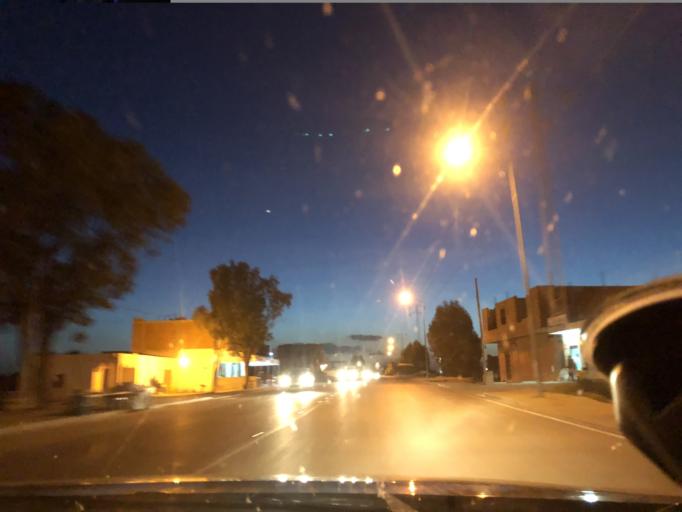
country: TN
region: Al Qasrayn
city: Kasserine
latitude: 35.2546
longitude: 9.0197
